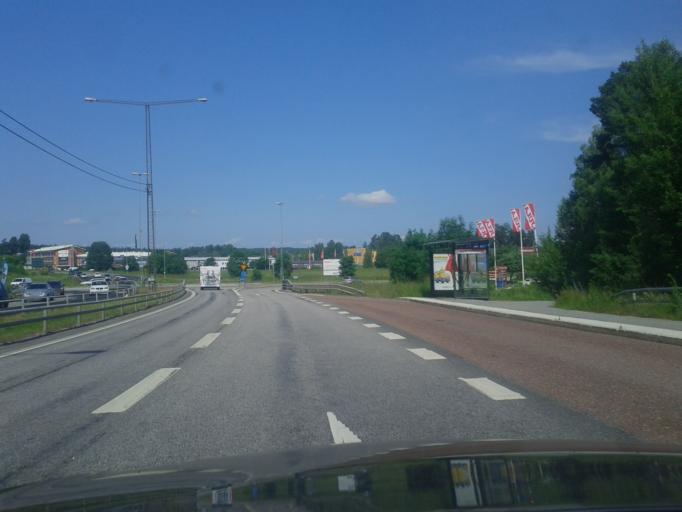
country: SE
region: Stockholm
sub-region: Taby Kommun
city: Taby
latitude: 59.4600
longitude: 18.1311
